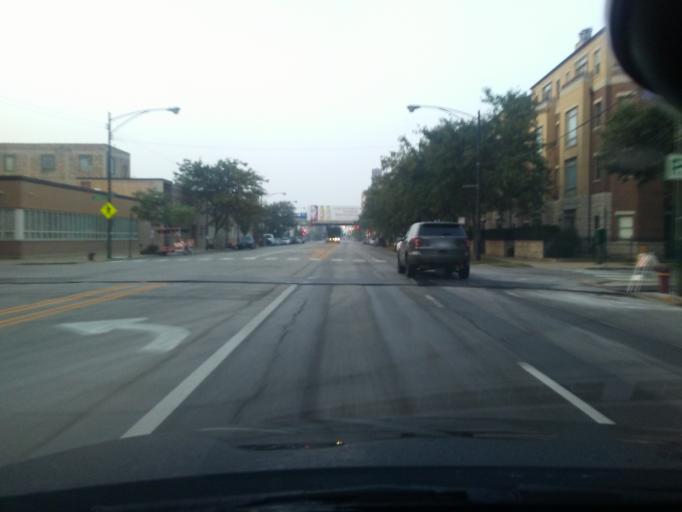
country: US
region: Illinois
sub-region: Cook County
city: Lincolnwood
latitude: 41.9453
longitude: -87.6689
